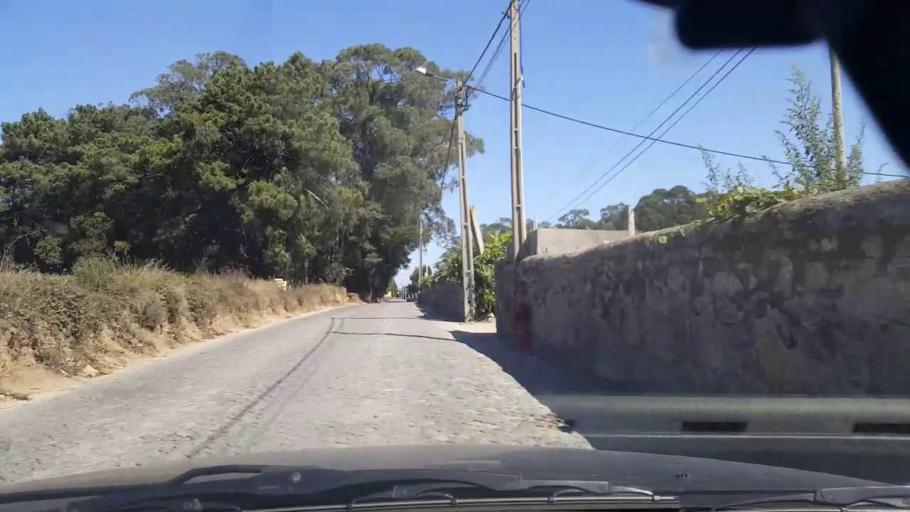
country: PT
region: Porto
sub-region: Vila do Conde
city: Arvore
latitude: 41.3179
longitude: -8.7065
